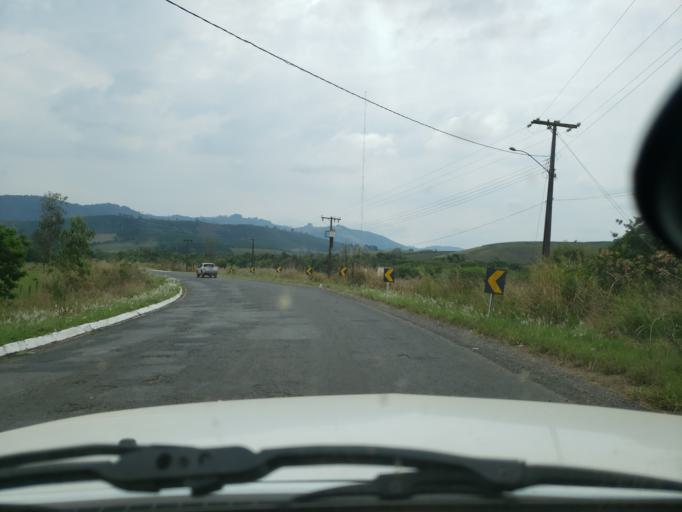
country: BR
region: Minas Gerais
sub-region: Jacutinga
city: Jacutinga
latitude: -22.2745
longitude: -46.6036
